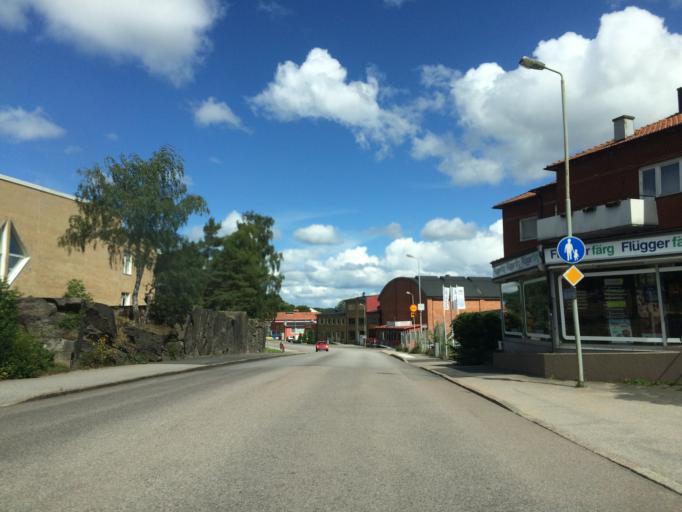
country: SE
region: Vaestra Goetaland
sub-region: Trollhattan
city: Trollhattan
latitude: 58.2819
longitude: 12.3020
